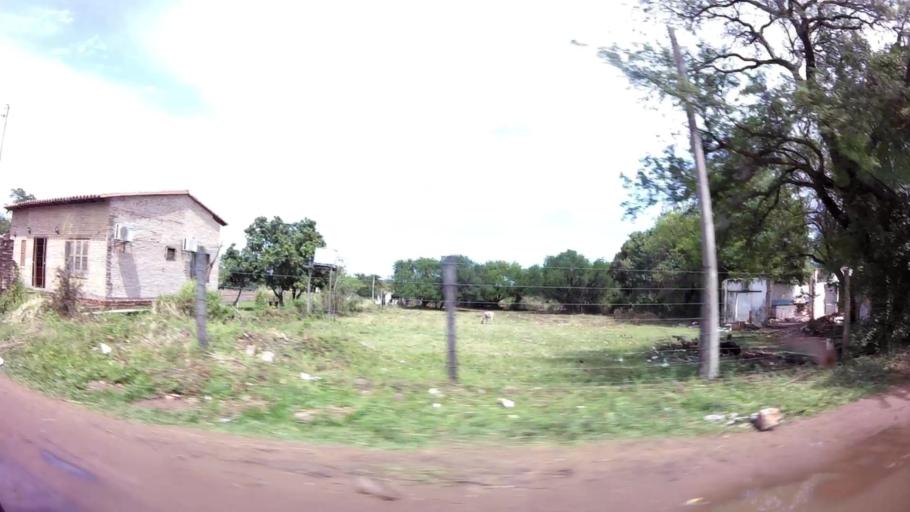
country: PY
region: Central
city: Limpio
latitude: -25.1629
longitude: -57.4780
